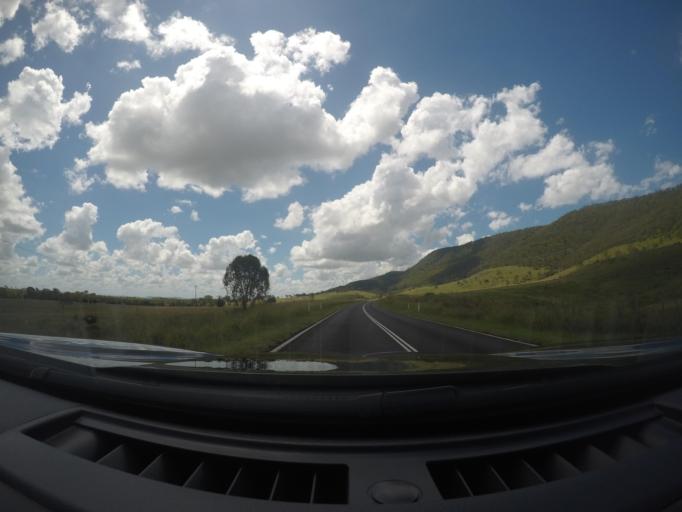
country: AU
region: Queensland
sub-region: Moreton Bay
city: Woodford
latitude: -27.1468
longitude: 152.5260
